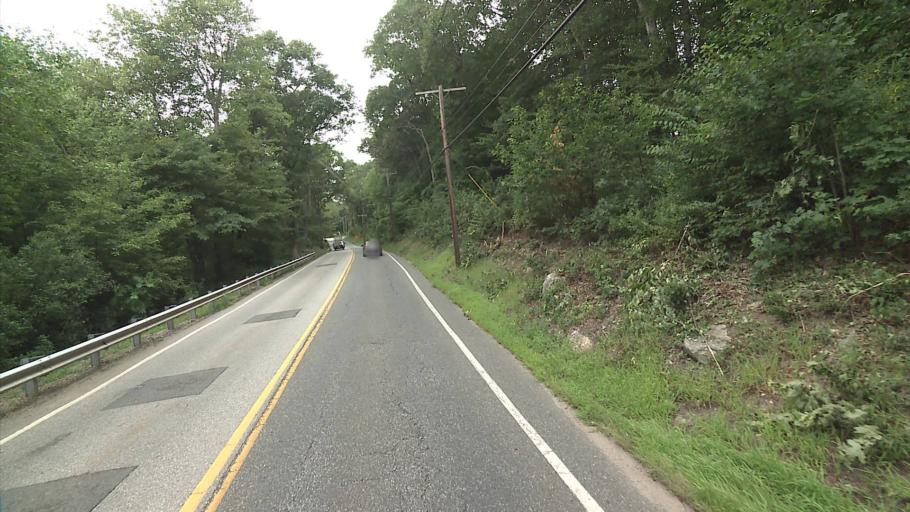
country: US
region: Connecticut
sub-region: New London County
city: Niantic
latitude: 41.3029
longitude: -72.2582
